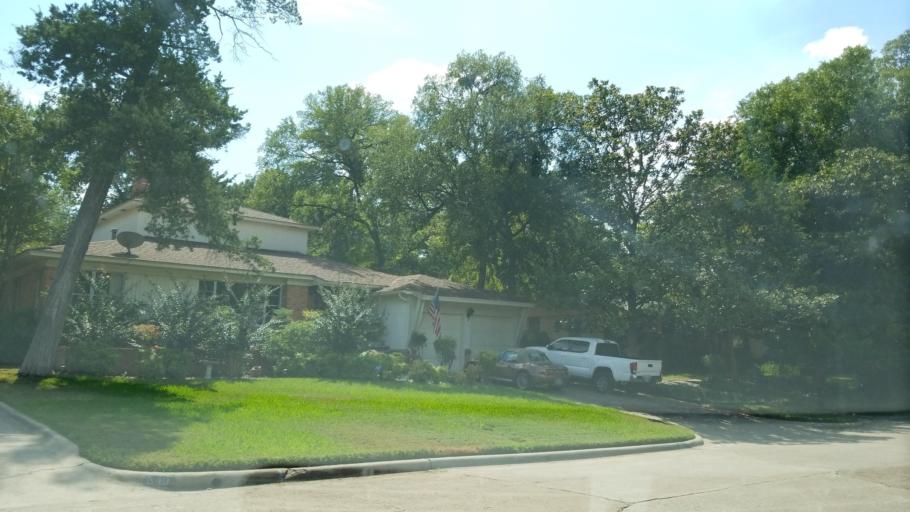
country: US
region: Texas
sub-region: Dallas County
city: Dallas
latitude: 32.7639
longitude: -96.8376
